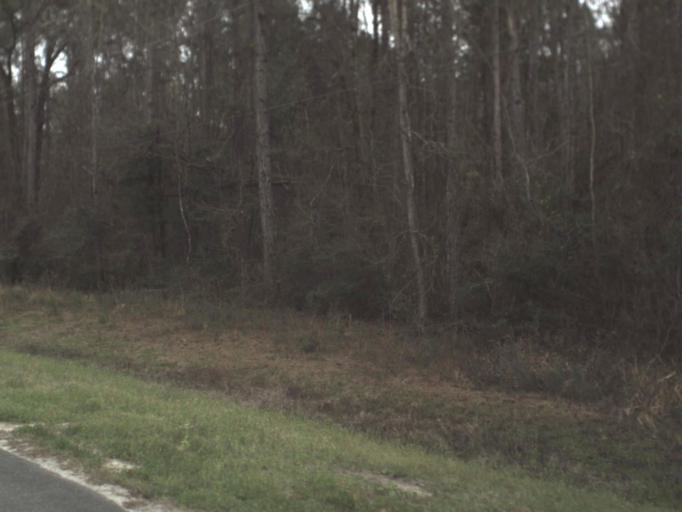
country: US
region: Florida
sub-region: Wakulla County
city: Crawfordville
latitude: 30.2571
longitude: -84.3484
